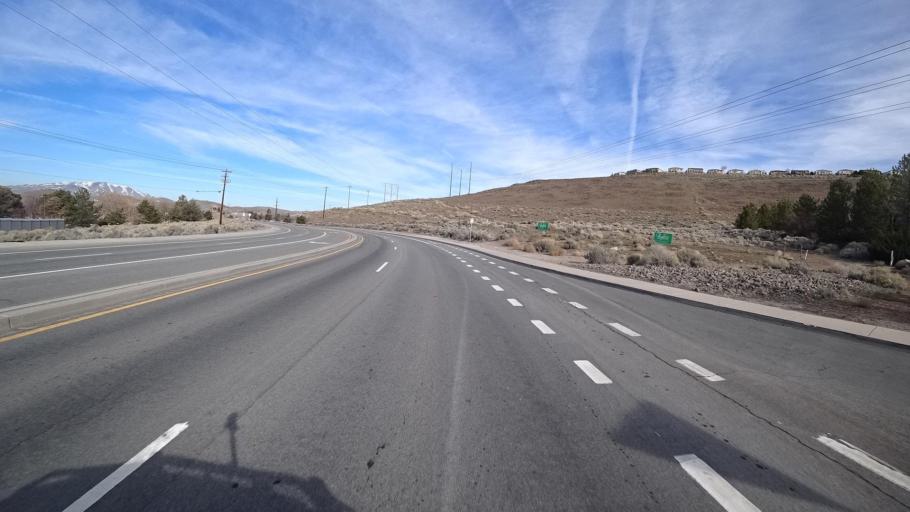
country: US
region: Nevada
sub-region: Washoe County
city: Sparks
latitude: 39.5645
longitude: -119.7057
